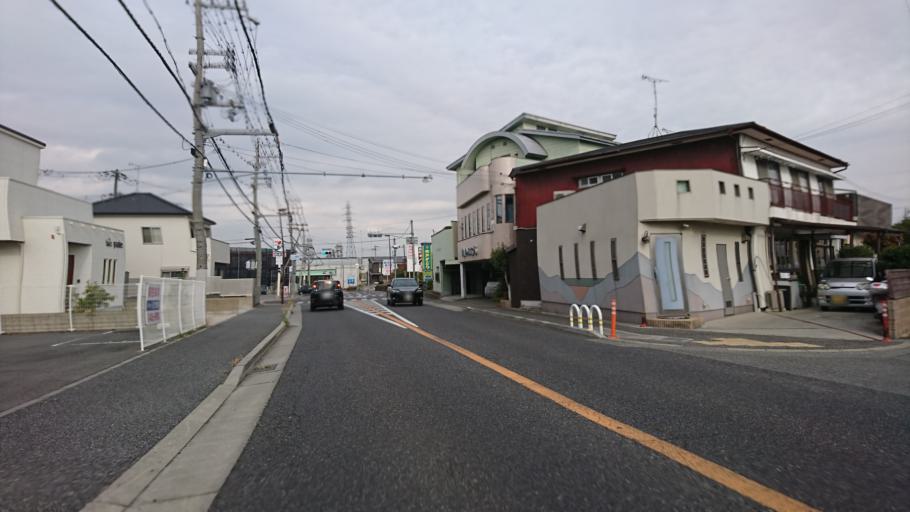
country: JP
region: Hyogo
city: Kakogawacho-honmachi
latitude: 34.7578
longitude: 134.8561
